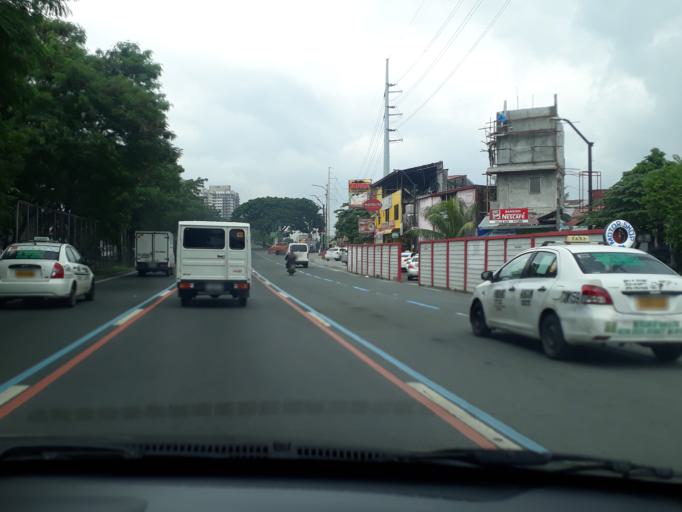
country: PH
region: Calabarzon
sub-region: Province of Rizal
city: Pateros
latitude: 14.5353
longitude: 121.0575
